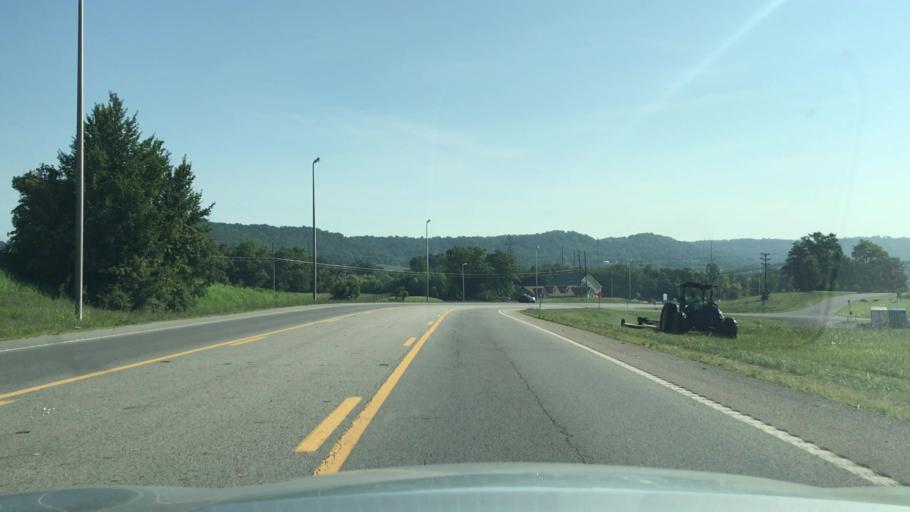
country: US
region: Tennessee
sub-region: Overton County
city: Livingston
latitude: 36.3923
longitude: -85.3322
